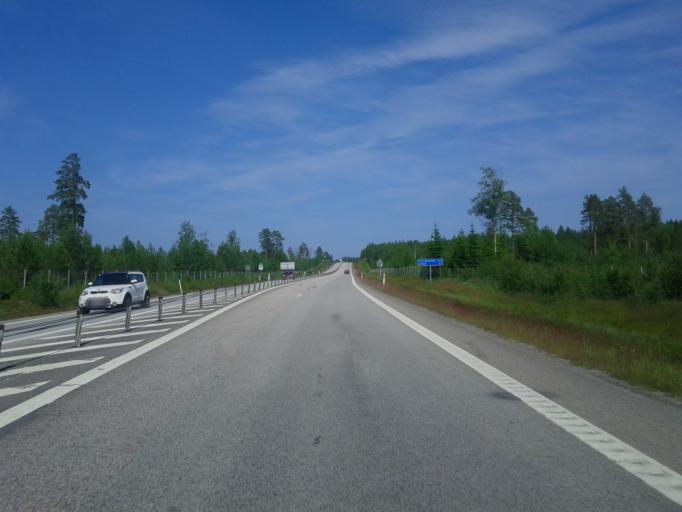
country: SE
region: Vaesterbotten
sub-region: Umea Kommun
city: Hoernefors
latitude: 63.6422
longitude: 19.9266
